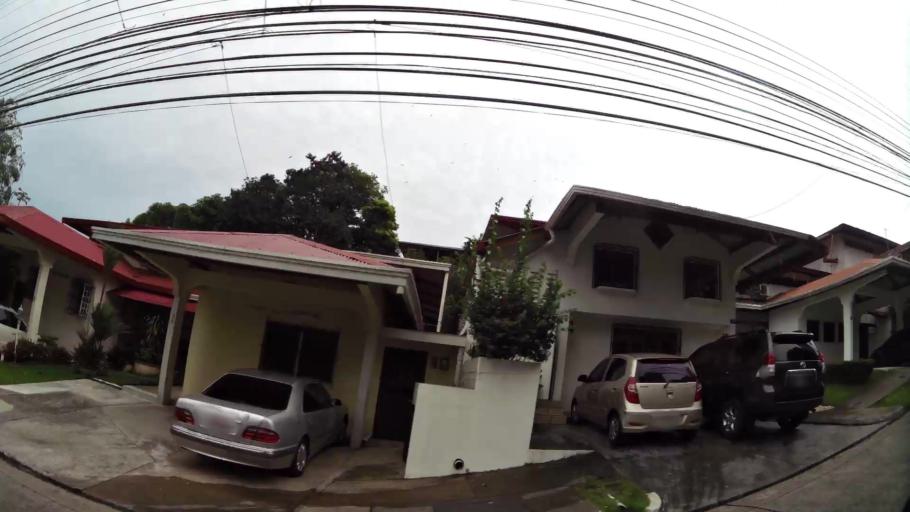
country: PA
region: Panama
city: Panama
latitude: 9.0170
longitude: -79.5327
